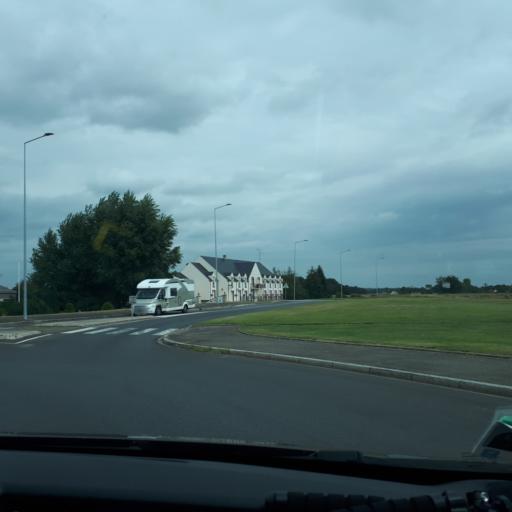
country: FR
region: Centre
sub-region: Departement du Loiret
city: Saint-Pere-sur-Loire
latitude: 47.7723
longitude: 2.3721
